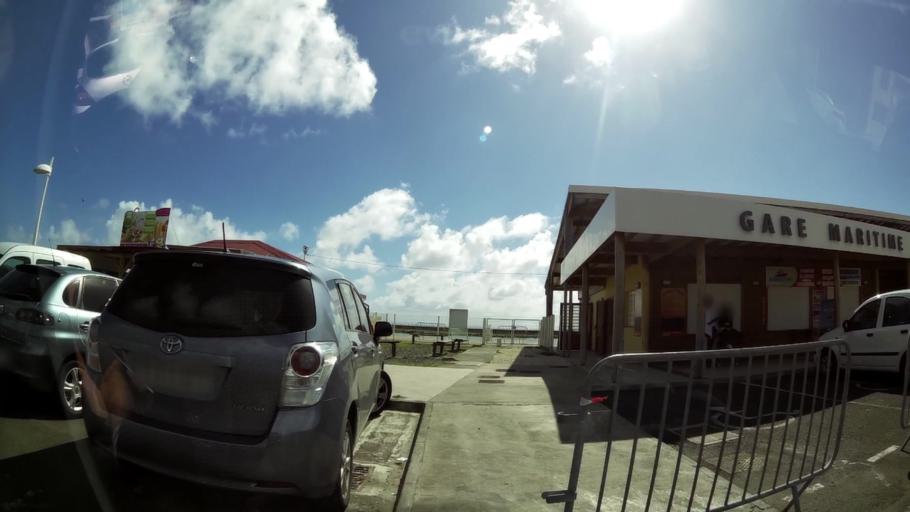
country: GP
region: Guadeloupe
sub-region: Guadeloupe
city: Saint-Francois
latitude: 16.2504
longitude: -61.2729
